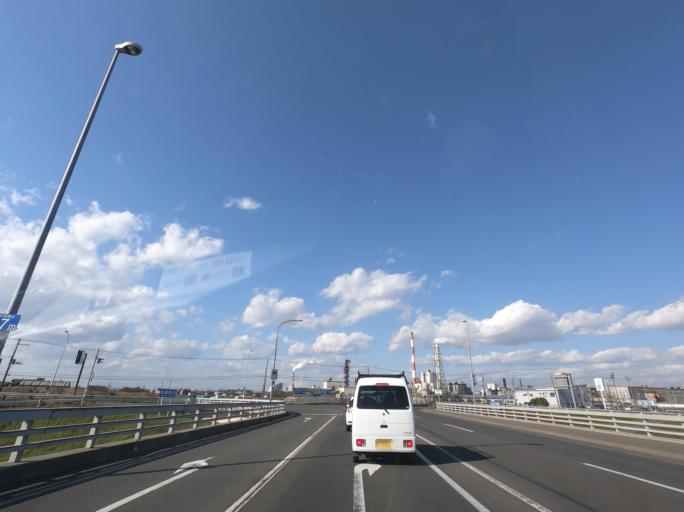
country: JP
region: Hokkaido
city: Kushiro
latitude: 43.0005
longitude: 144.3600
